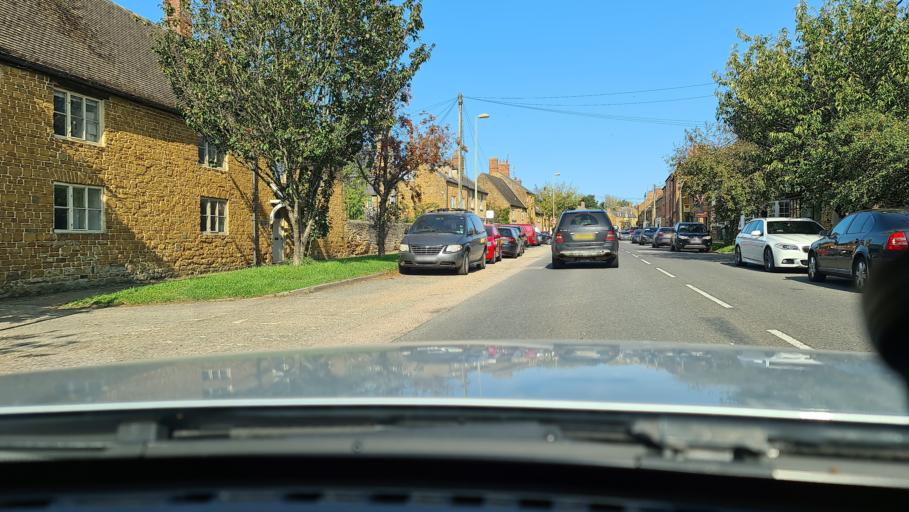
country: GB
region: England
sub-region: Oxfordshire
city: Deddington
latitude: 51.9794
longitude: -1.3222
